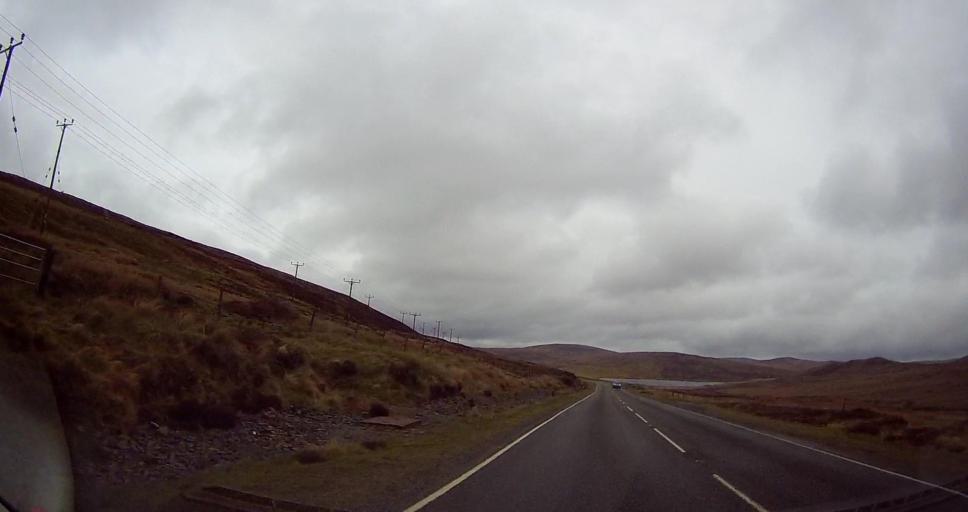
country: GB
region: Scotland
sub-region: Shetland Islands
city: Lerwick
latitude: 60.3336
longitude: -1.2538
